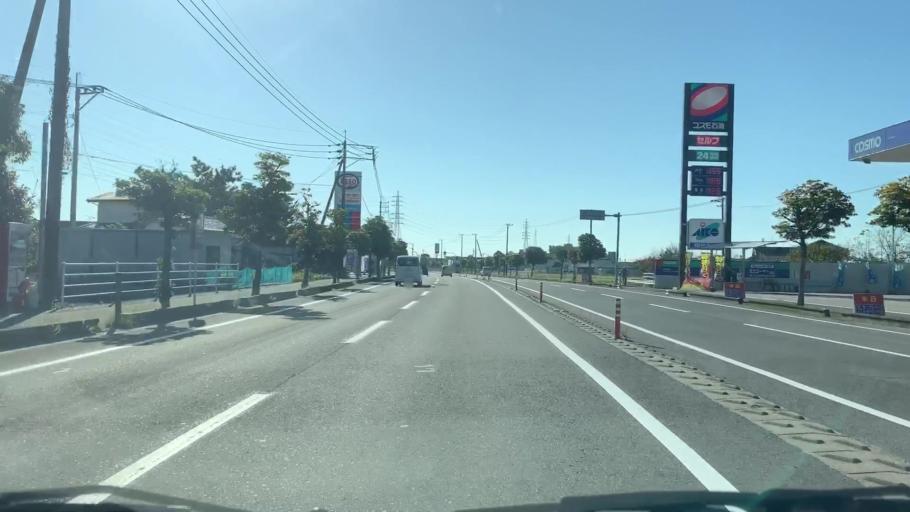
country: JP
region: Saga Prefecture
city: Saga-shi
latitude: 33.2989
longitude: 130.2809
